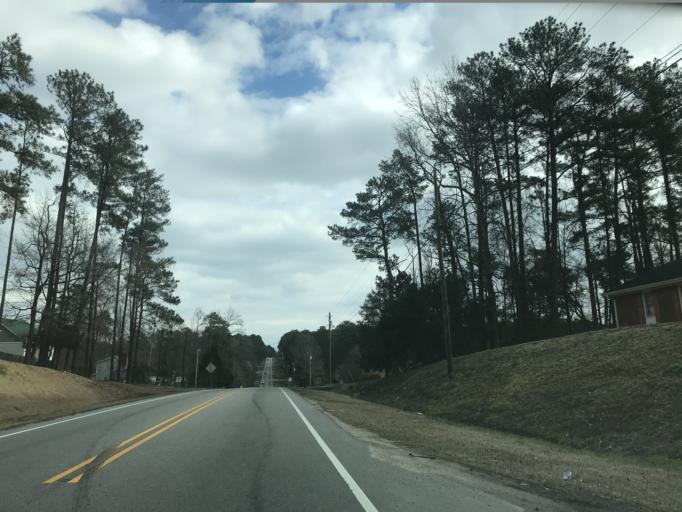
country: US
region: North Carolina
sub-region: Wake County
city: Raleigh
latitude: 35.8116
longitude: -78.5883
